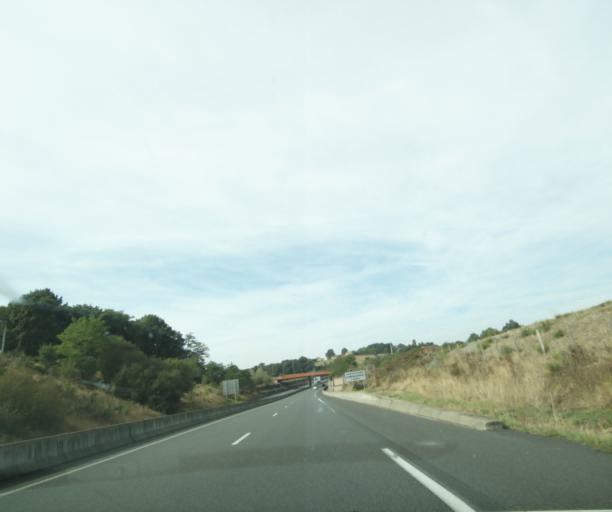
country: FR
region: Auvergne
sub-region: Departement de l'Allier
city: Lapalisse
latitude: 46.2360
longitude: 3.6344
